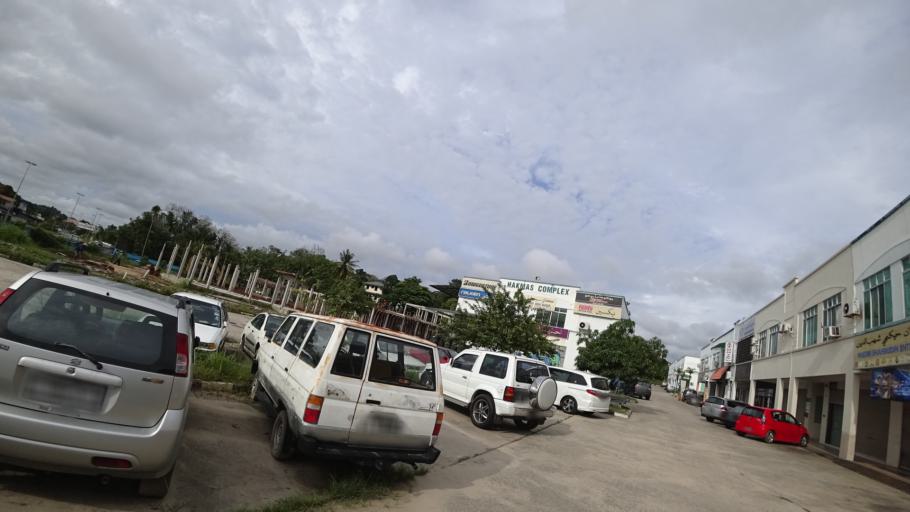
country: BN
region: Brunei and Muara
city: Bandar Seri Begawan
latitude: 4.8847
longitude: 114.8587
